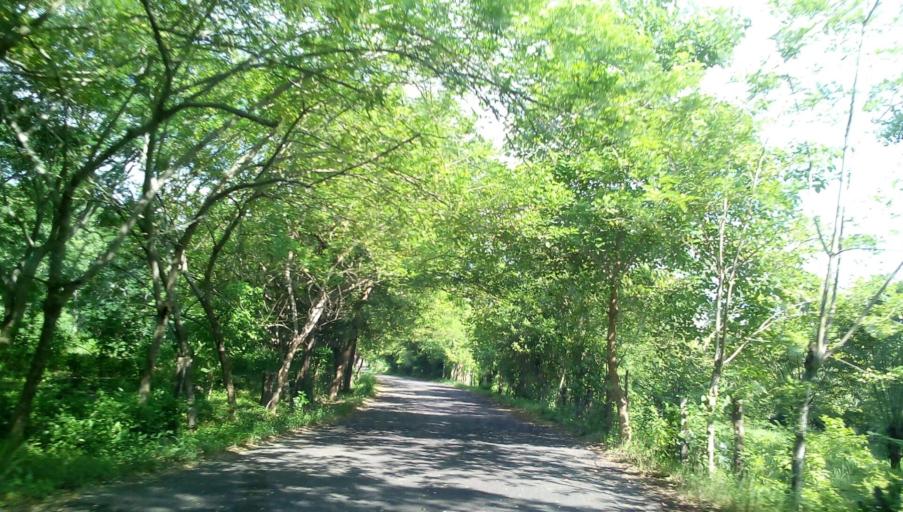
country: MX
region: Veracruz
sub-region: Citlaltepetl
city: Las Sabinas
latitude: 21.3542
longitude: -97.8978
